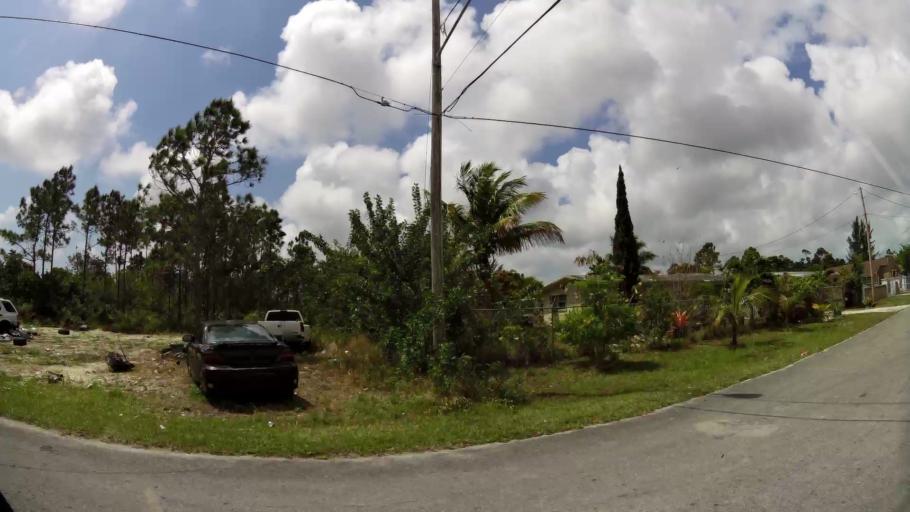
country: BS
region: Freeport
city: Lucaya
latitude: 26.5434
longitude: -78.6463
